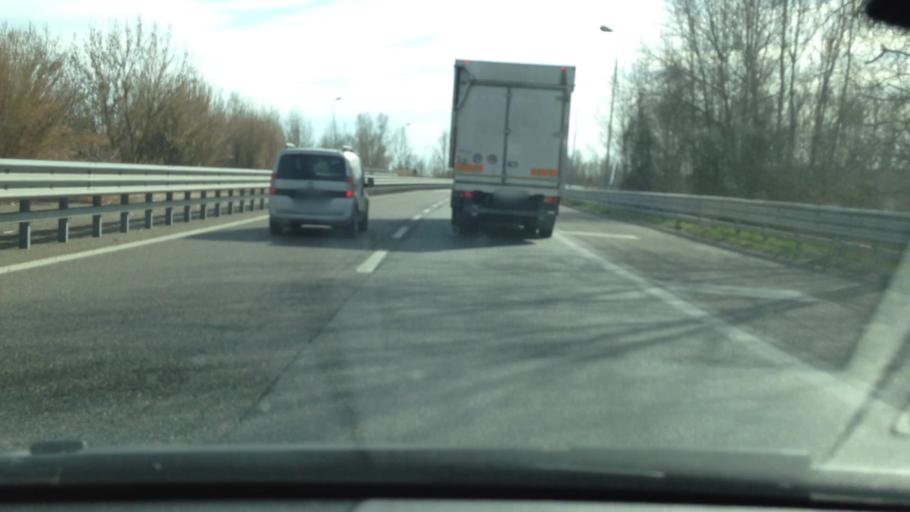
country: IT
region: Piedmont
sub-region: Provincia di Asti
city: Castell'Alfero
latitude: 44.9605
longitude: 8.2285
